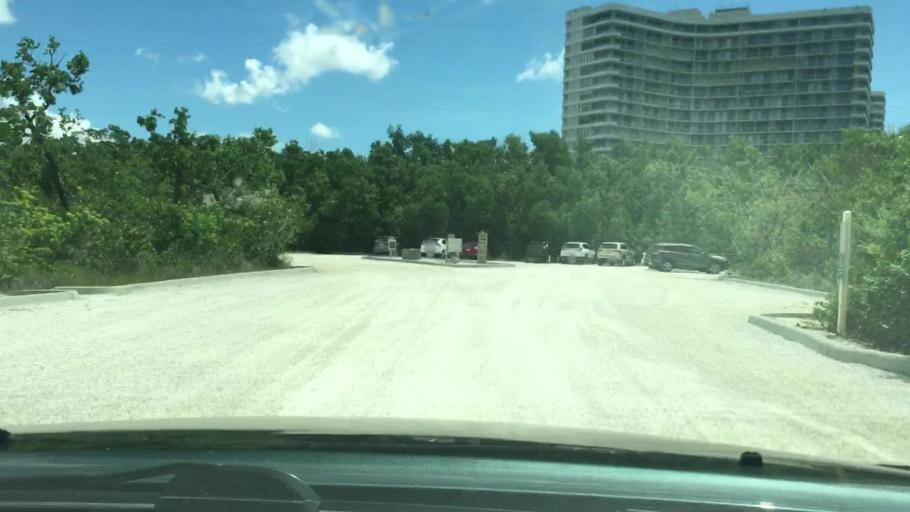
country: US
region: Florida
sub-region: Collier County
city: Marco
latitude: 25.9473
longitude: -81.7413
